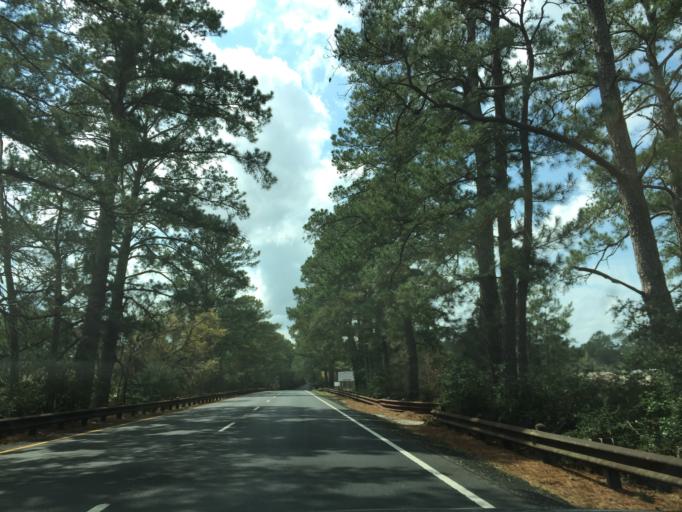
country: US
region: Texas
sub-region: Bastrop County
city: Bastrop
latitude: 30.1161
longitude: -97.2833
